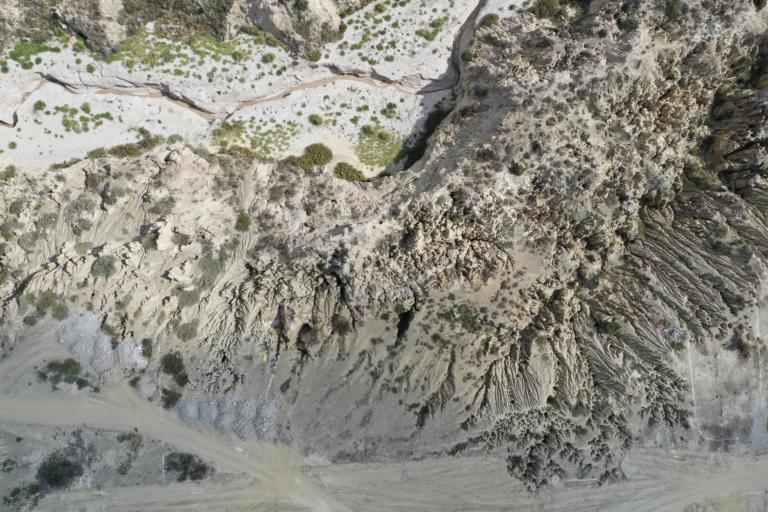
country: BO
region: La Paz
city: La Paz
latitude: -16.5643
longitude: -68.1212
